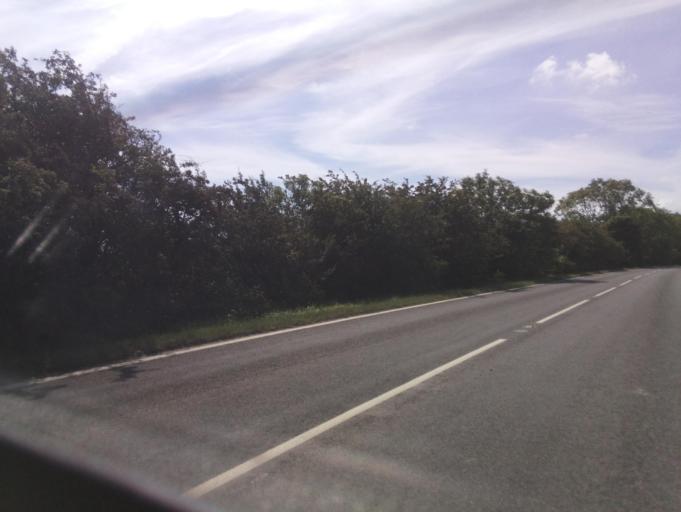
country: GB
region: England
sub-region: North Lincolnshire
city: Manton
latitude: 53.5027
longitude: -0.5820
